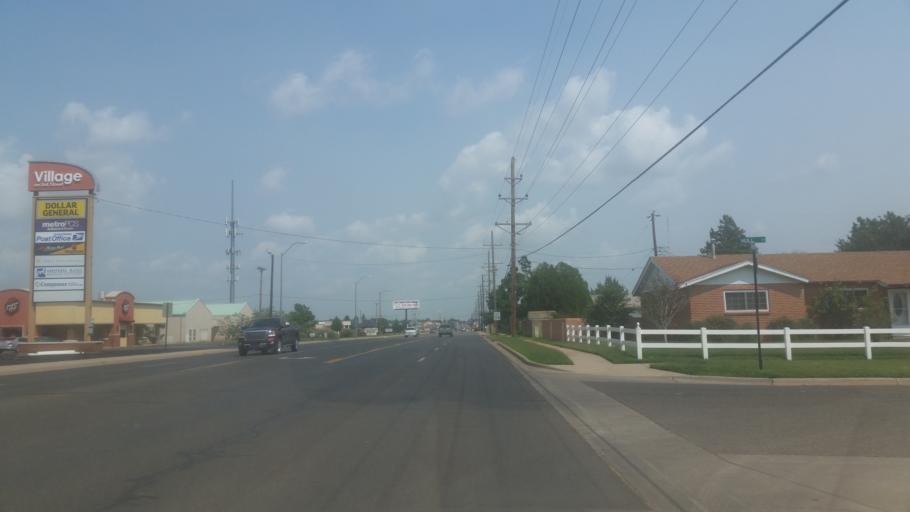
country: US
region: New Mexico
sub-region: Curry County
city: Clovis
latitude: 34.4192
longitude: -103.2202
